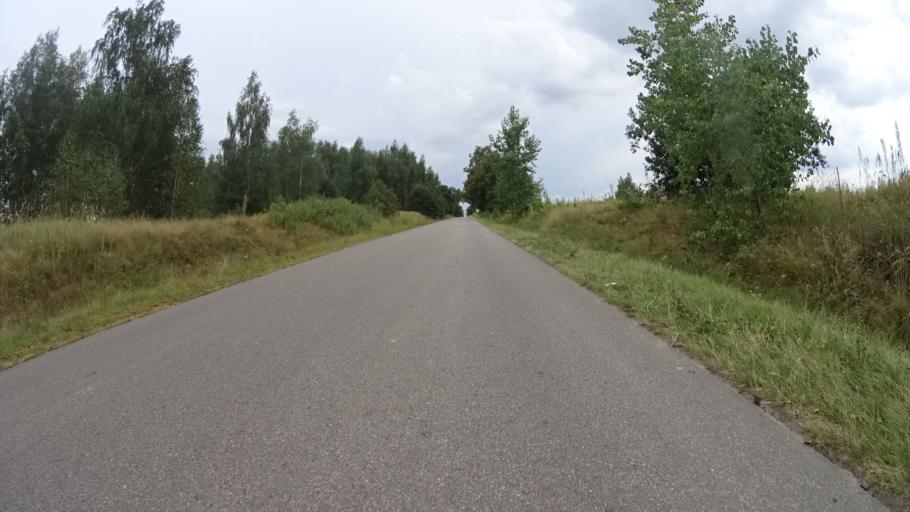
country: PL
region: Masovian Voivodeship
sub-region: Powiat grojecki
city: Goszczyn
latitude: 51.6706
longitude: 20.8571
